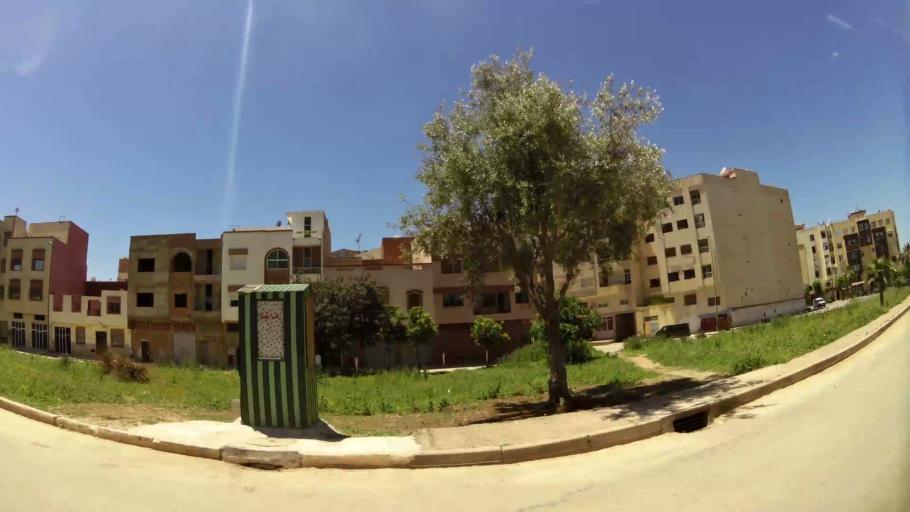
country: MA
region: Meknes-Tafilalet
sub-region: Meknes
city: Meknes
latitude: 33.8669
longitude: -5.5752
